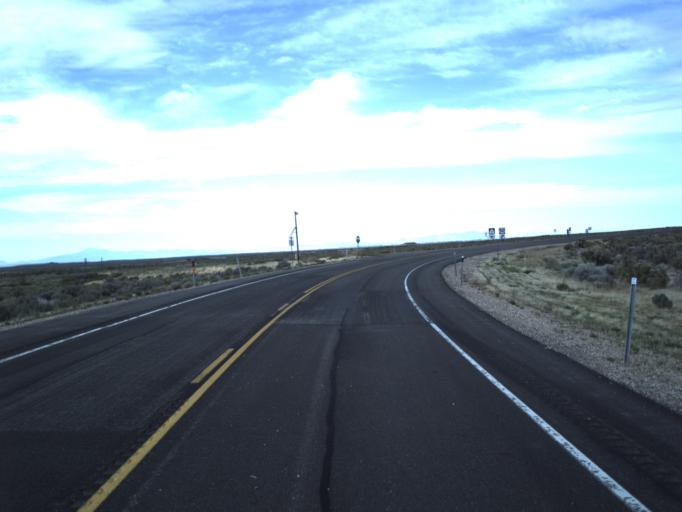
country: US
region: Utah
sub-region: Millard County
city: Fillmore
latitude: 39.1554
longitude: -112.4075
